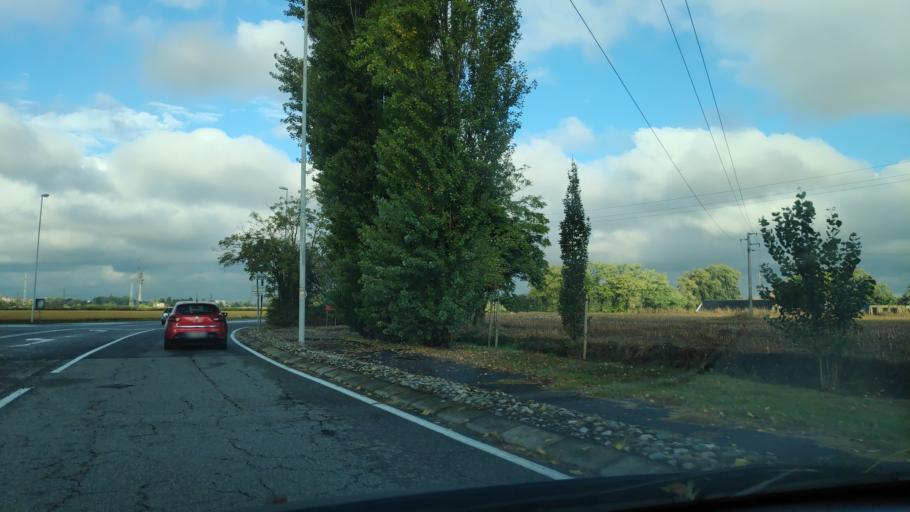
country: IT
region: Lombardy
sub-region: Citta metropolitana di Milano
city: Opera
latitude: 45.3825
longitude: 9.2082
